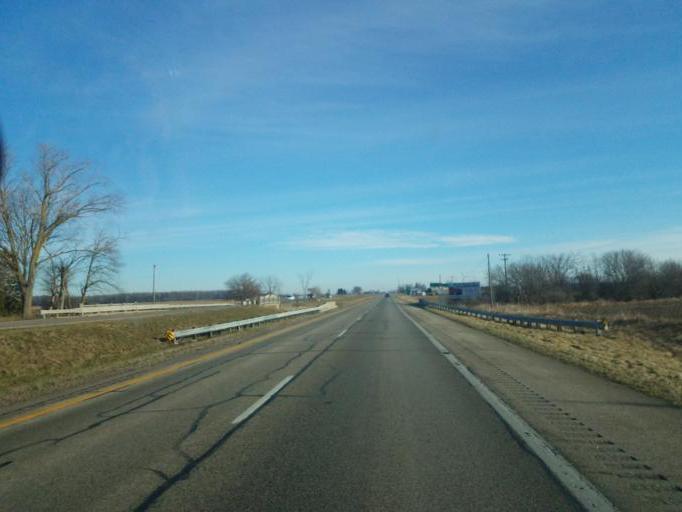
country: US
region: Michigan
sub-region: Gratiot County
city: Ithaca
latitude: 43.2439
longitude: -84.5631
